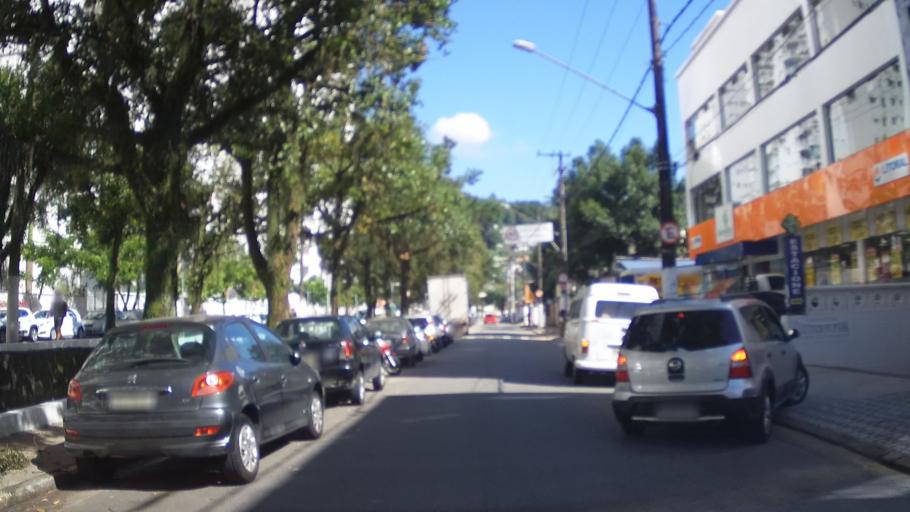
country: BR
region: Sao Paulo
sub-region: Santos
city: Santos
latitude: -23.9578
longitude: -46.3496
